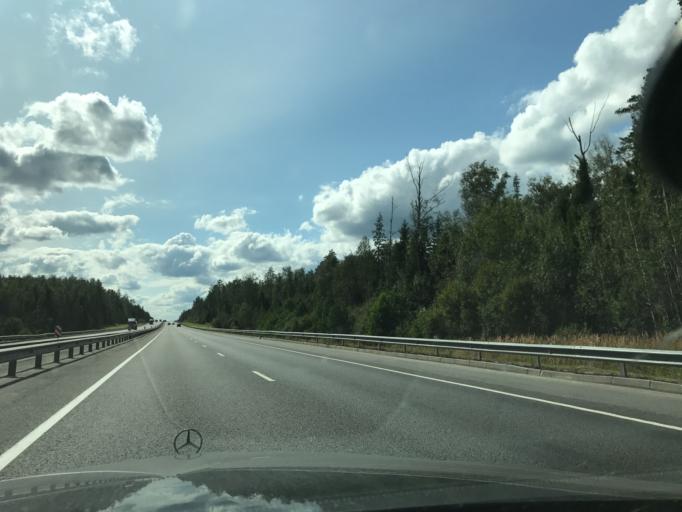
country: RU
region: Vladimir
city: Sudogda
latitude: 56.1459
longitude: 40.9099
